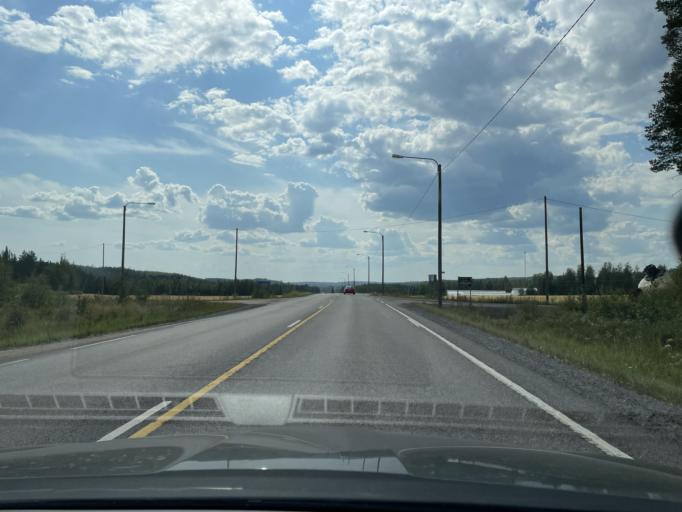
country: FI
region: Central Finland
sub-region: Jyvaeskylae
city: Korpilahti
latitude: 61.9874
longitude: 25.4203
